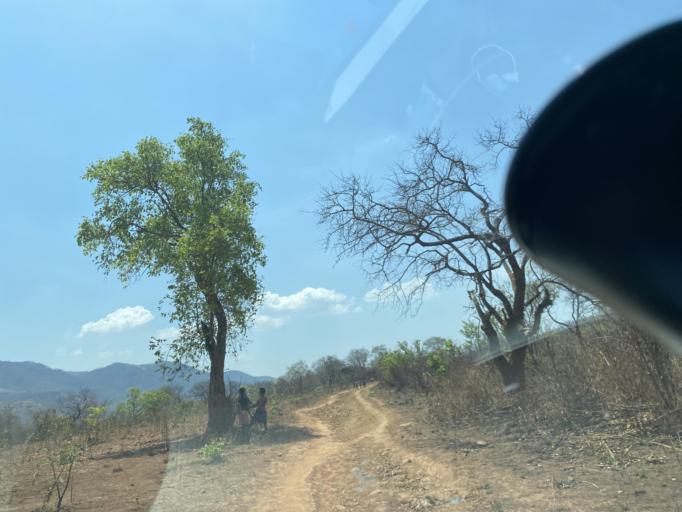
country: ZM
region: Lusaka
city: Kafue
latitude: -15.7831
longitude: 28.4604
